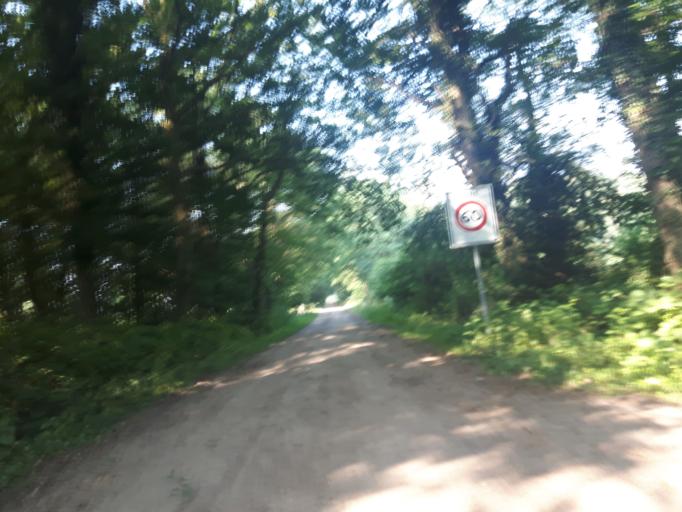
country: NL
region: Overijssel
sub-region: Gemeente Hengelo
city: Hengelo
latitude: 52.1916
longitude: 6.8063
